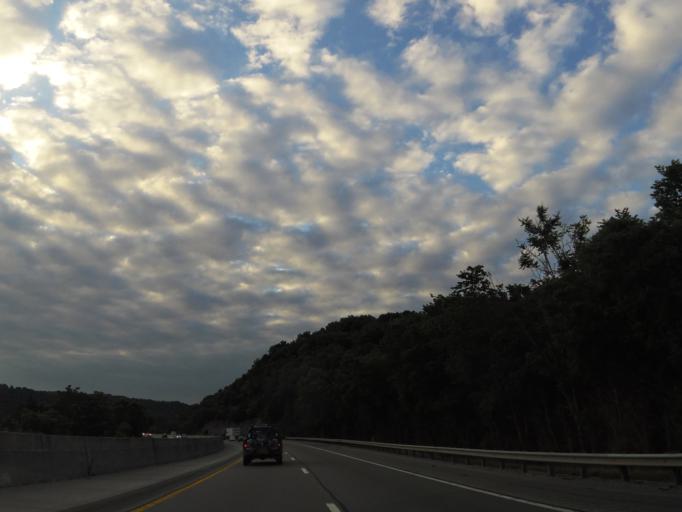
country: US
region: Tennessee
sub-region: Putnam County
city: Lafayette
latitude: 36.1117
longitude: -85.7709
